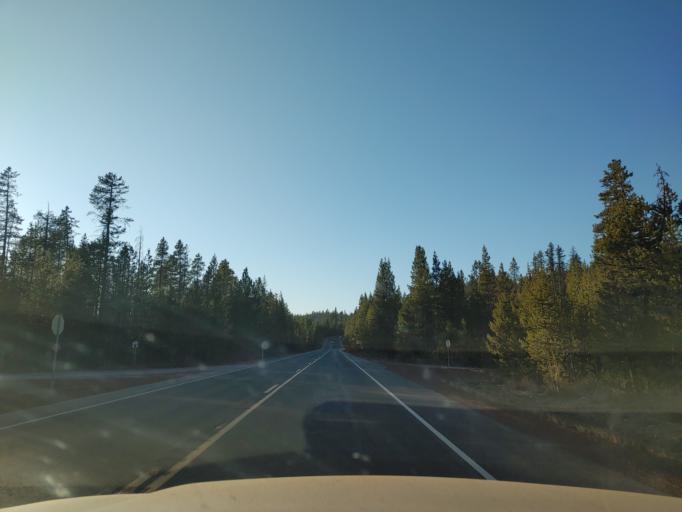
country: US
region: Oregon
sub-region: Deschutes County
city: La Pine
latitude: 43.4401
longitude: -121.8649
